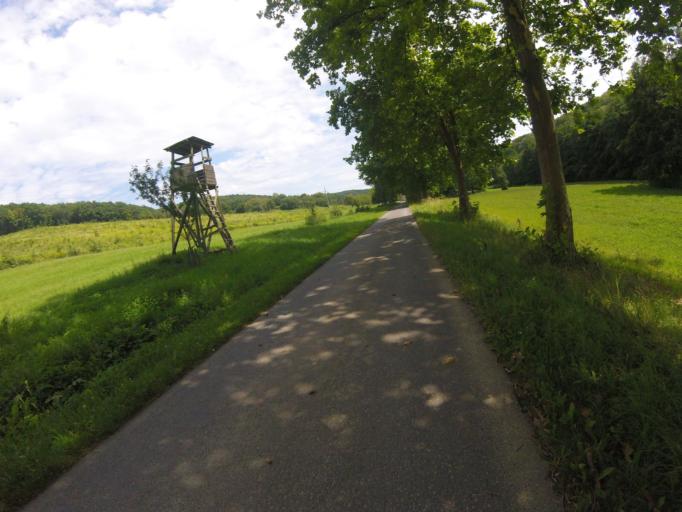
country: HU
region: Zala
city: Lenti
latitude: 46.5622
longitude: 16.6360
